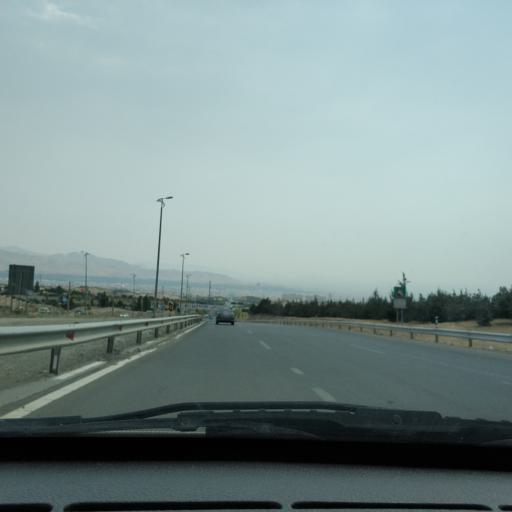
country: IR
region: Tehran
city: Tajrish
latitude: 35.7845
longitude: 51.5650
